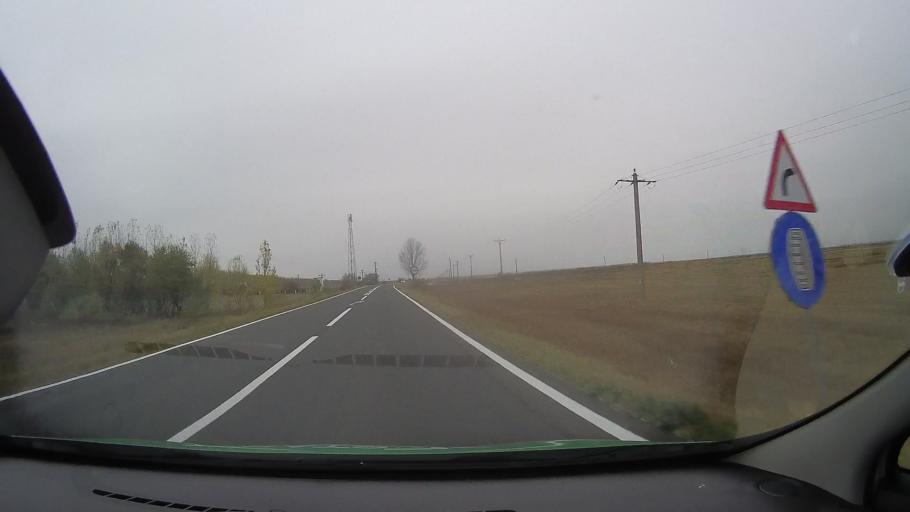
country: RO
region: Ialomita
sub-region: Comuna Giurgeni
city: Giurgeni
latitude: 44.7253
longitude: 27.8535
